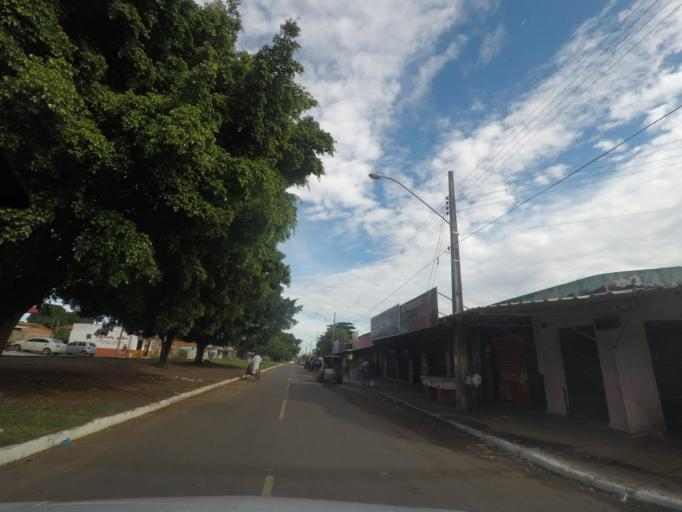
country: BR
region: Goias
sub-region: Aparecida De Goiania
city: Aparecida de Goiania
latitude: -16.8213
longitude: -49.3102
